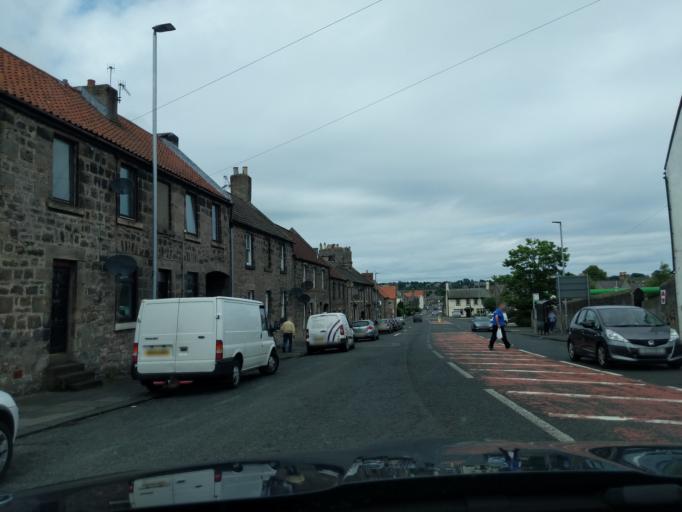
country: GB
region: England
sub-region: Northumberland
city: Berwick-Upon-Tweed
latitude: 55.7615
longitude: -2.0104
